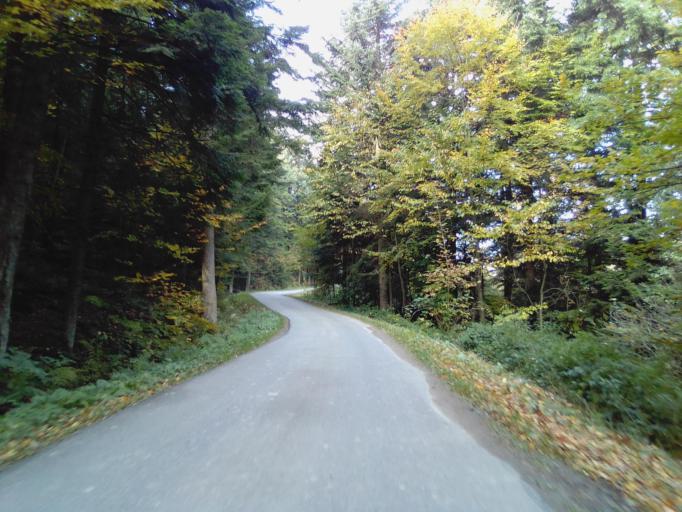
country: PL
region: Subcarpathian Voivodeship
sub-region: Powiat strzyzowski
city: Konieczkowa
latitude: 49.8537
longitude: 21.9596
